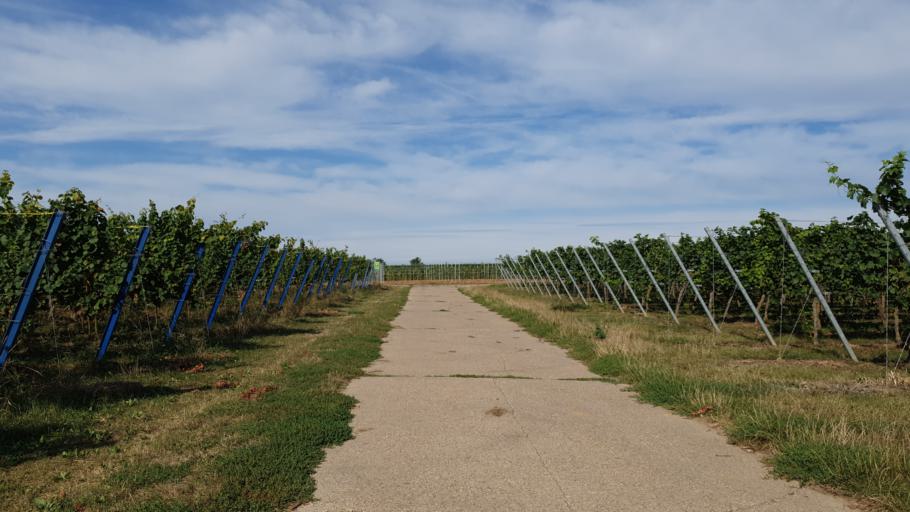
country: DE
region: Rheinland-Pfalz
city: Winden
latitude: 49.1183
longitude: 8.1075
